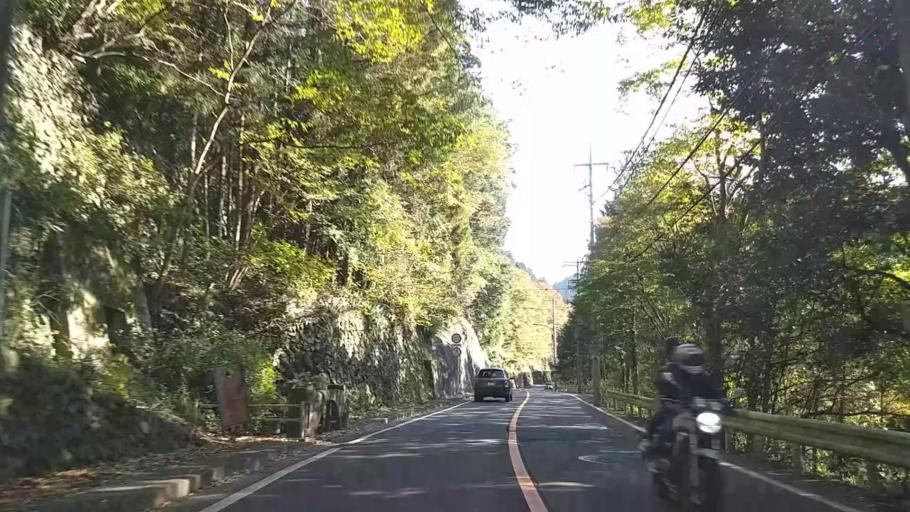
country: JP
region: Tokyo
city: Ome
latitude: 35.8106
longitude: 139.1685
